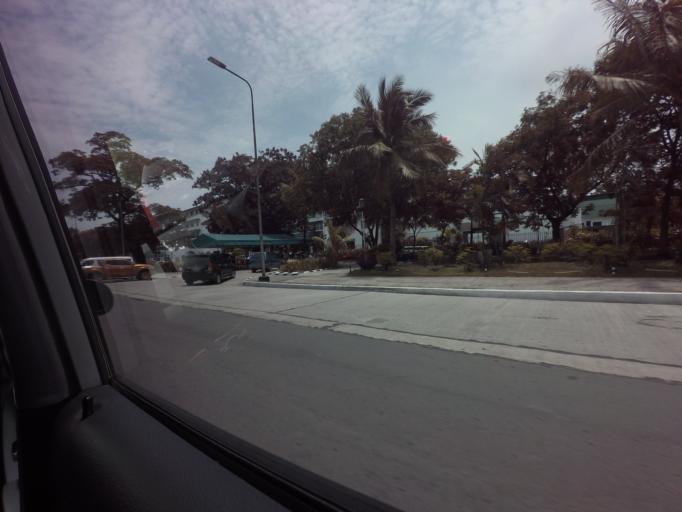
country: PH
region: Metro Manila
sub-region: City of Manila
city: Port Area
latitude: 14.5827
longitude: 120.9749
